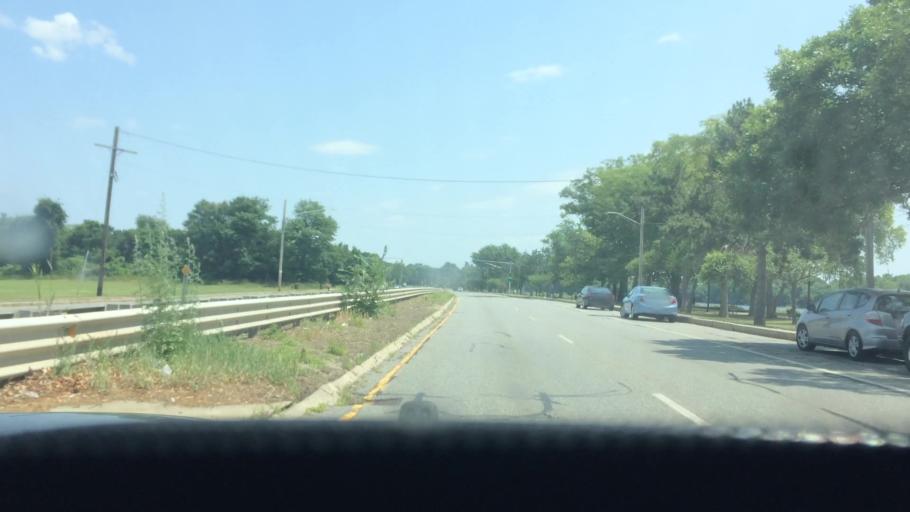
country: US
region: Massachusetts
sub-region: Middlesex County
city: Lowell
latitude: 42.6408
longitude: -71.3507
